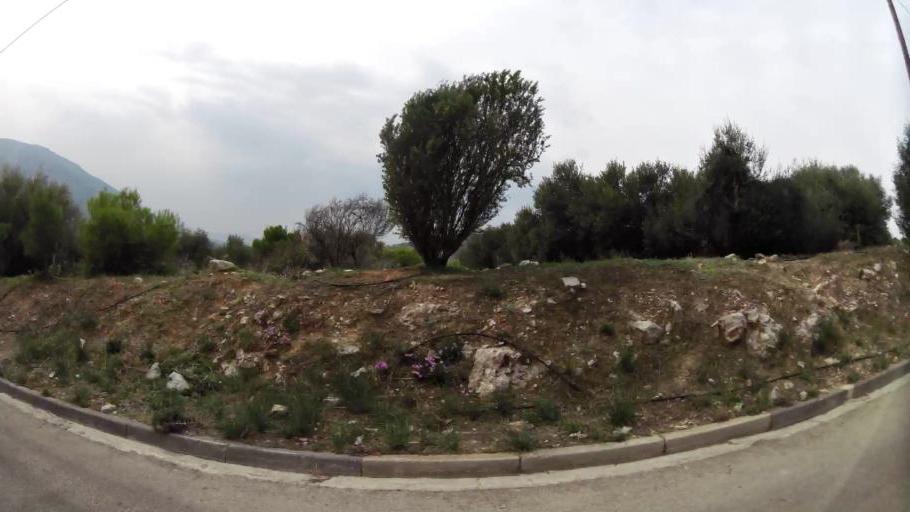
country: GR
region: Attica
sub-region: Nomarchia Athinas
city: Chaidari
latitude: 38.0192
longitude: 23.6414
